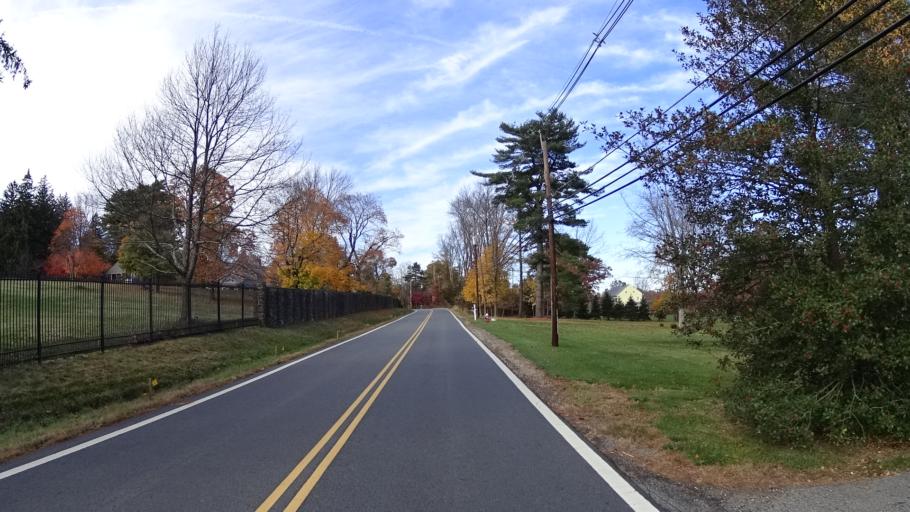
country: US
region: New Jersey
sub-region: Morris County
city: Madison
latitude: 40.7557
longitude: -74.4531
